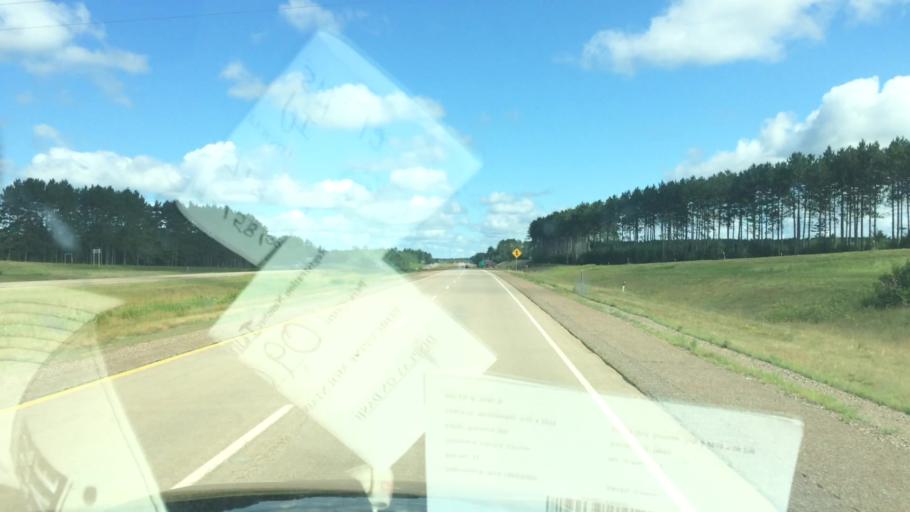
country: US
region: Wisconsin
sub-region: Lincoln County
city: Tomahawk
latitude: 45.4708
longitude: -89.6913
